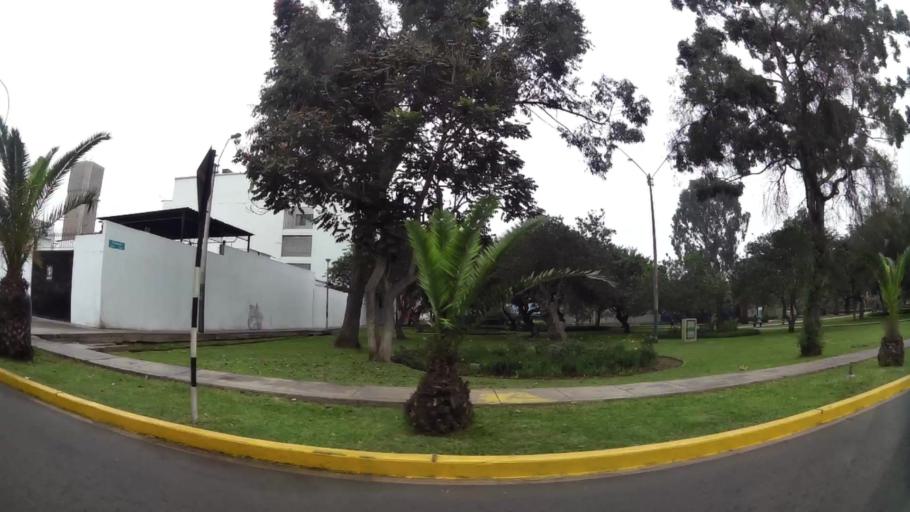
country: PE
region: Lima
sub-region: Lima
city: San Luis
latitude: -12.1058
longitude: -77.0077
